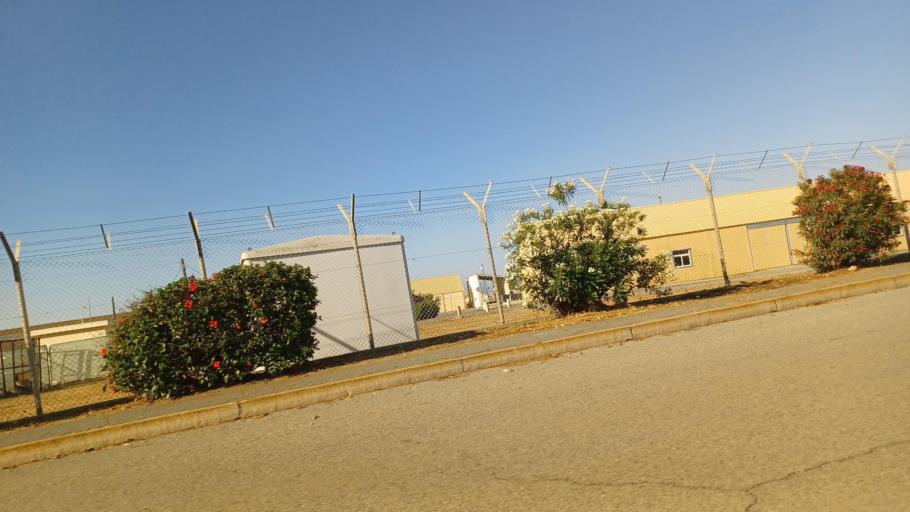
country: CY
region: Larnaka
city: Xylotymbou
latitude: 35.0007
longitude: 33.7400
